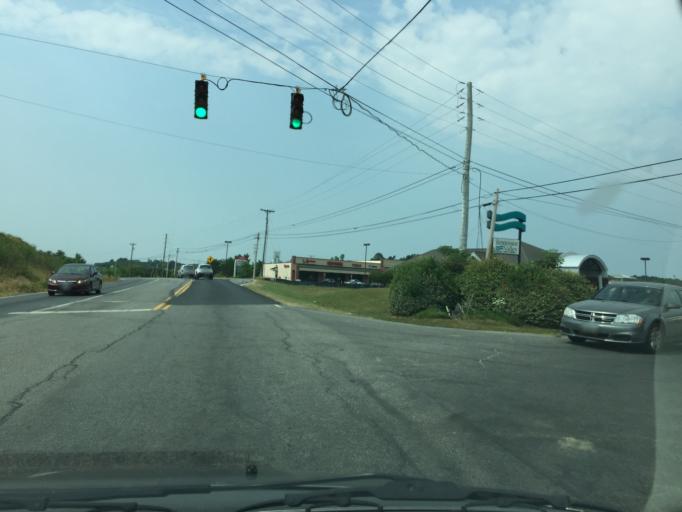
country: US
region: Georgia
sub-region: Catoosa County
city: Ringgold
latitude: 34.9064
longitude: -85.1306
